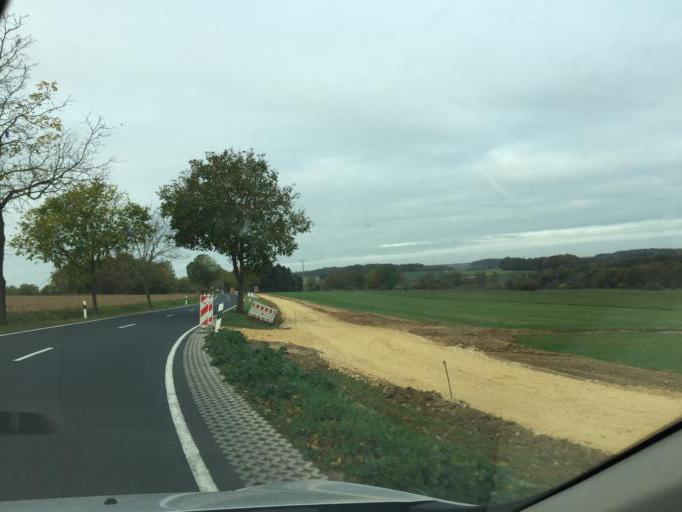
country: LU
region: Luxembourg
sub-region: Canton de Capellen
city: Kehlen
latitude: 49.6791
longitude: 6.0497
